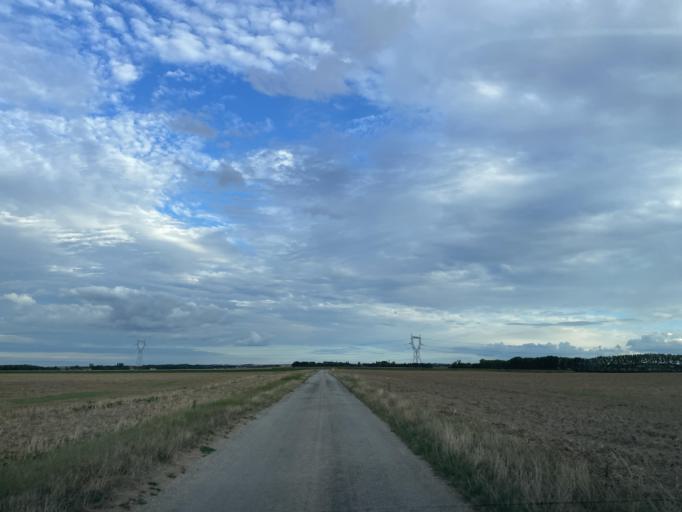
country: FR
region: Ile-de-France
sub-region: Departement de Seine-et-Marne
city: Gouaix
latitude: 48.4377
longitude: 3.3204
